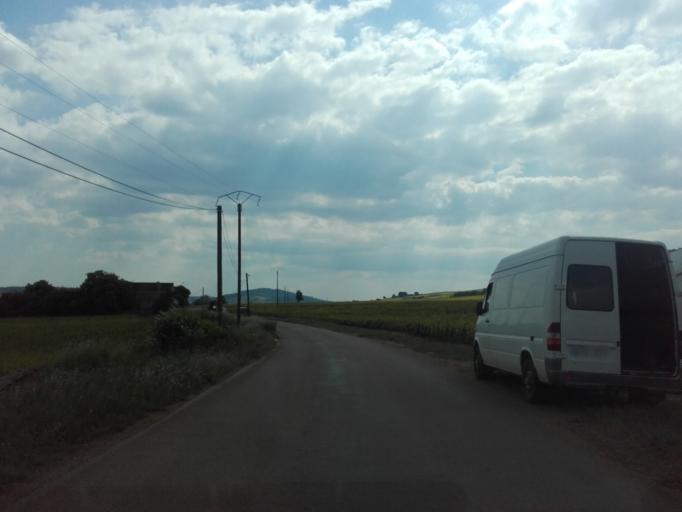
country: FR
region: Bourgogne
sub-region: Departement de la Cote-d'Or
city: Corpeau
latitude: 46.9319
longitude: 4.7261
